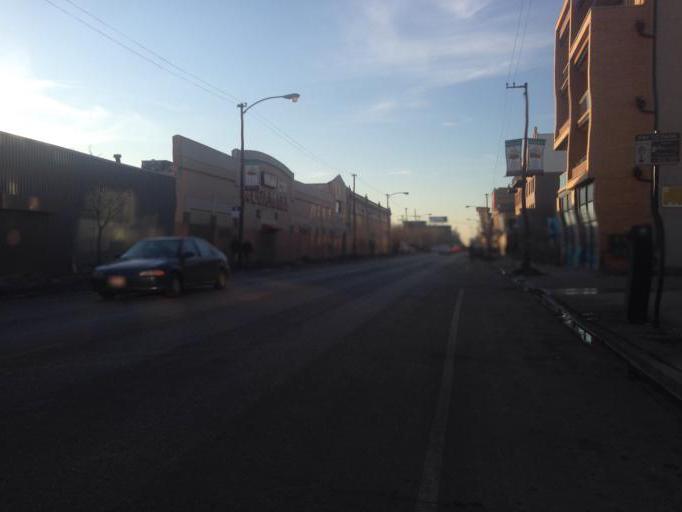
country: US
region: Illinois
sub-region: Cook County
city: Lincolnwood
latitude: 41.9264
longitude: -87.7029
